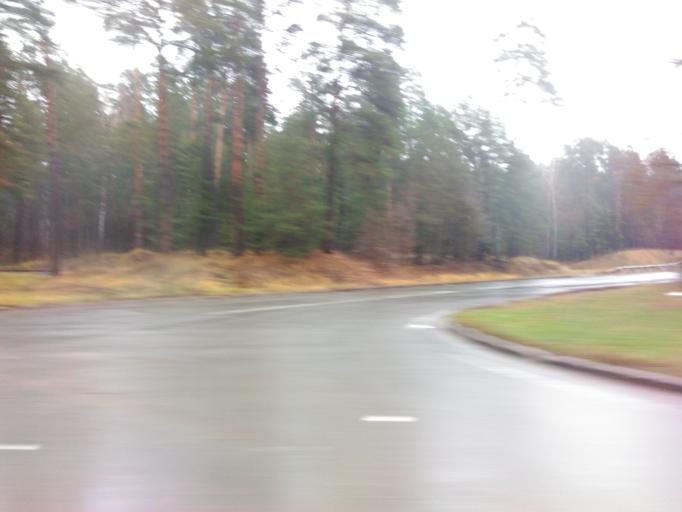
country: RU
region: Tatarstan
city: Osinovo
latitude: 55.8265
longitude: 48.8965
